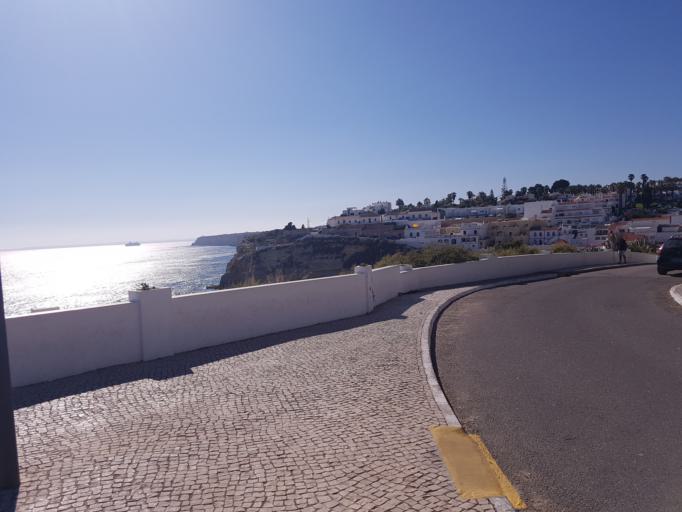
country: PT
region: Faro
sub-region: Lagoa
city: Carvoeiro
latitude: 37.0952
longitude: -8.4709
